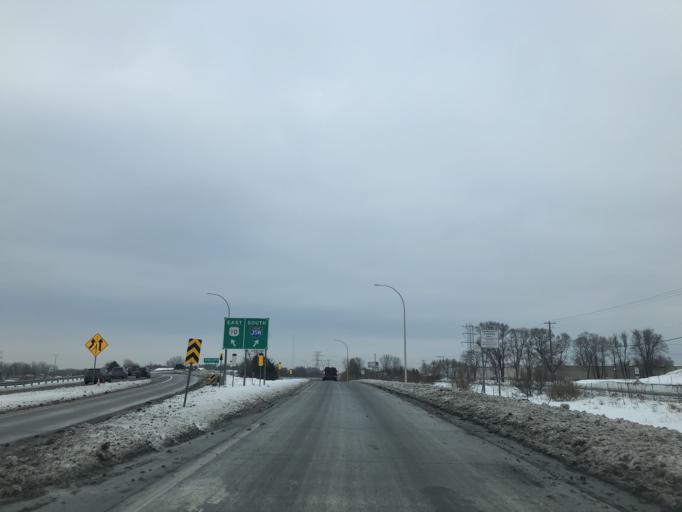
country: US
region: Minnesota
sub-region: Ramsey County
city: Mounds View
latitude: 45.0899
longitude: -93.1894
